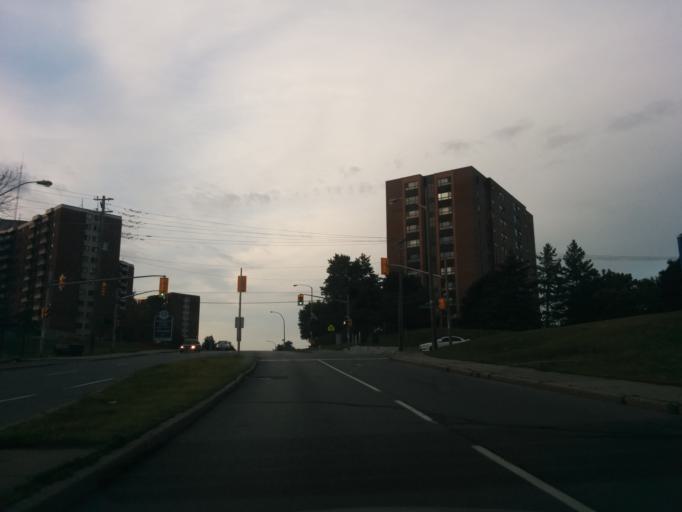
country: CA
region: Ontario
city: Ottawa
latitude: 45.3529
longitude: -75.7306
